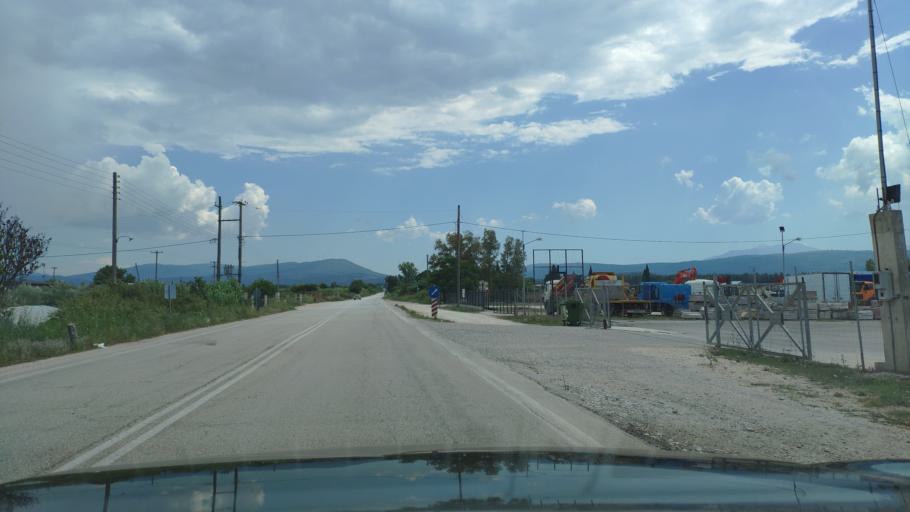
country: GR
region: West Greece
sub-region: Nomos Aitolias kai Akarnanias
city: Krikellos
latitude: 38.9436
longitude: 21.1766
